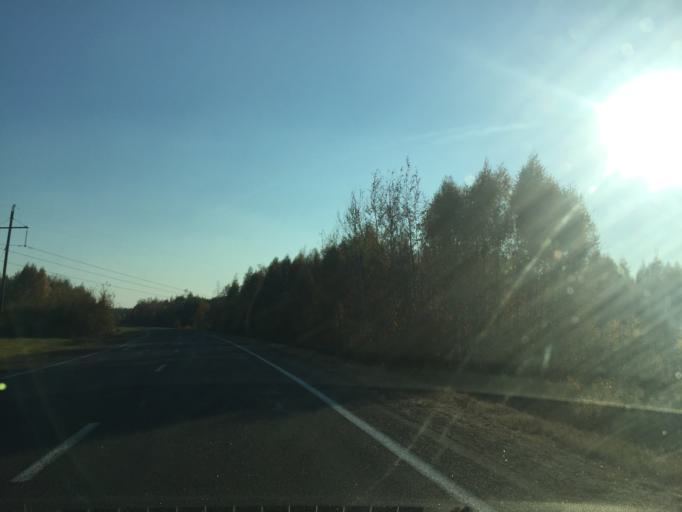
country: BY
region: Gomel
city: Dobrush
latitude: 52.3513
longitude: 31.2293
